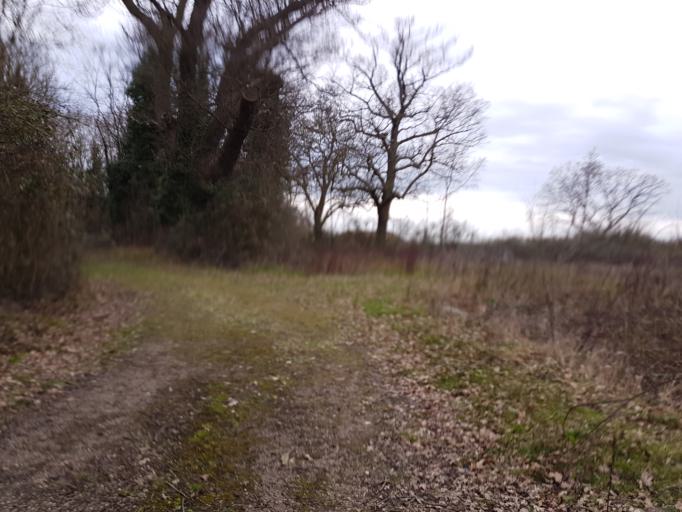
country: GB
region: England
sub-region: Cambridgeshire
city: Girton
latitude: 52.2346
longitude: 0.0548
